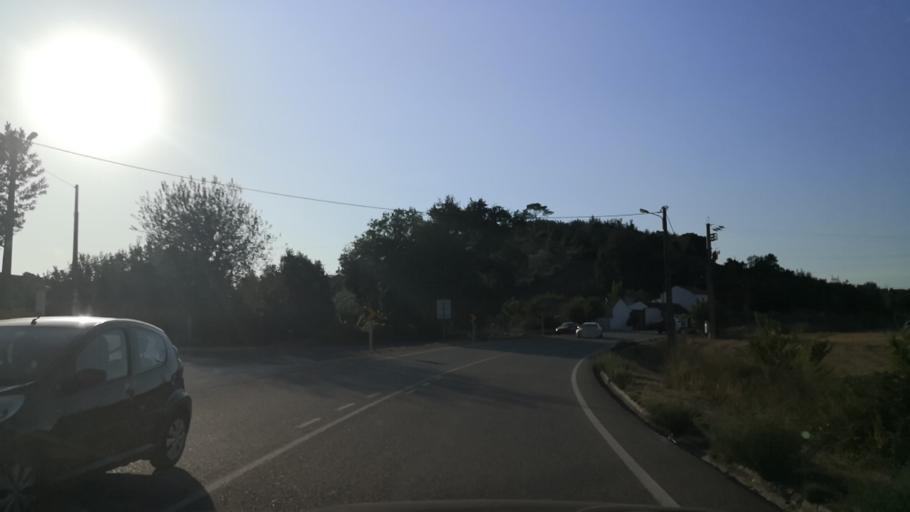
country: PT
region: Santarem
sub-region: Alcanena
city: Alcanena
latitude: 39.3659
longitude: -8.6559
